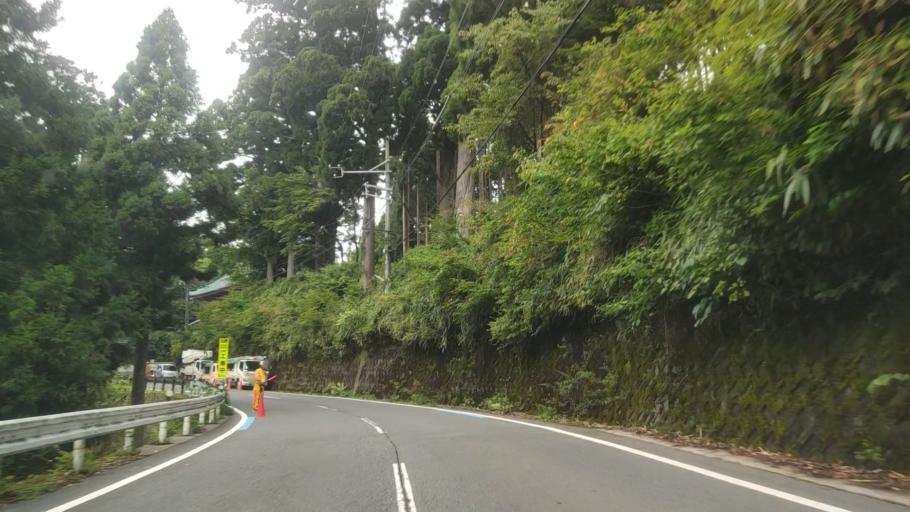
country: JP
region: Wakayama
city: Koya
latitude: 34.2120
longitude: 135.5725
